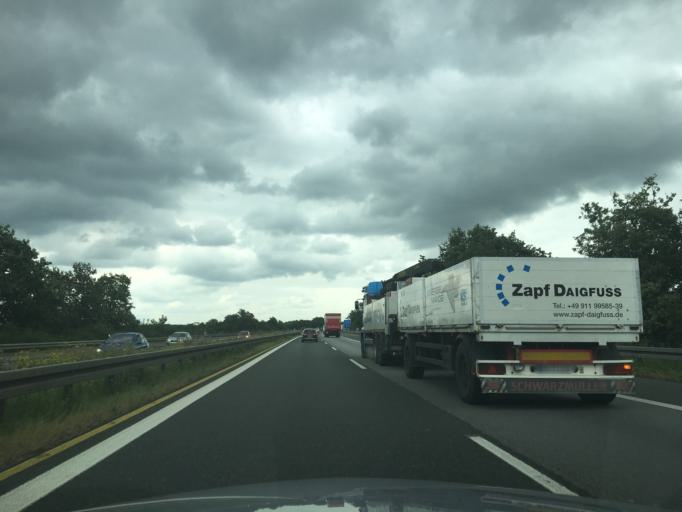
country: DE
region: Bavaria
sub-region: Regierungsbezirk Mittelfranken
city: Gremsdorf
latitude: 49.7043
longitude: 10.8520
